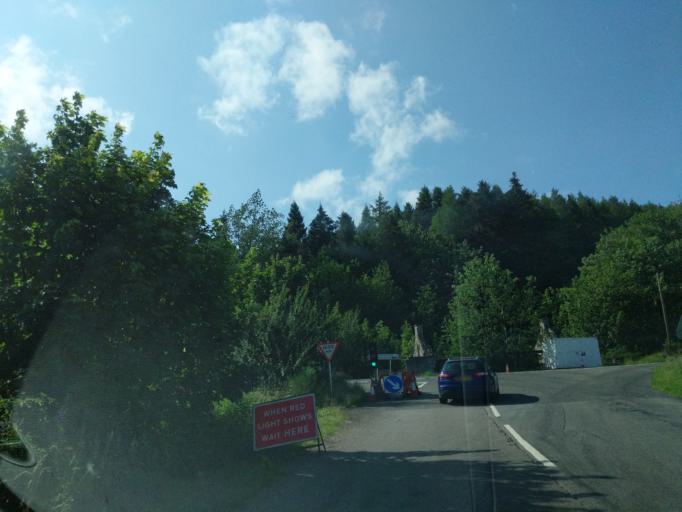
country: GB
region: Scotland
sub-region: Moray
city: Rothes
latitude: 57.5539
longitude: -3.1527
